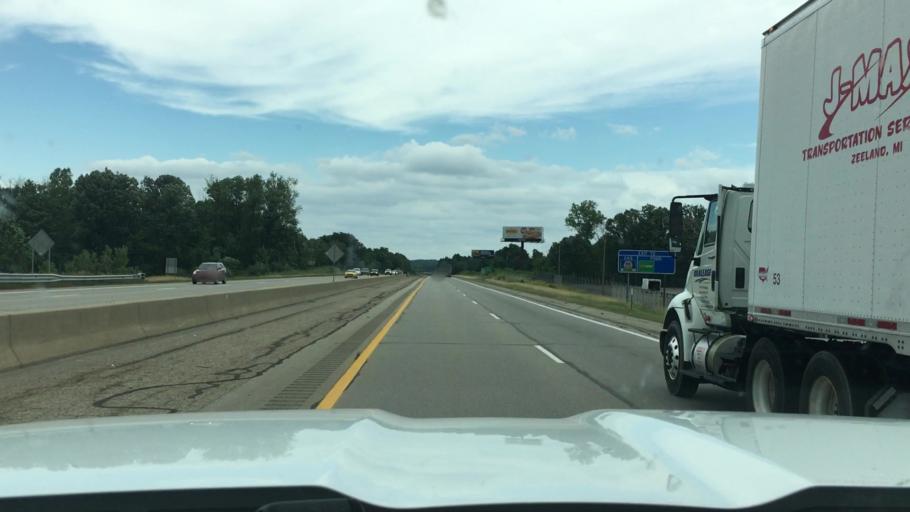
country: US
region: Michigan
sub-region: Kent County
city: Byron Center
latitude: 42.7662
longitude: -85.6723
